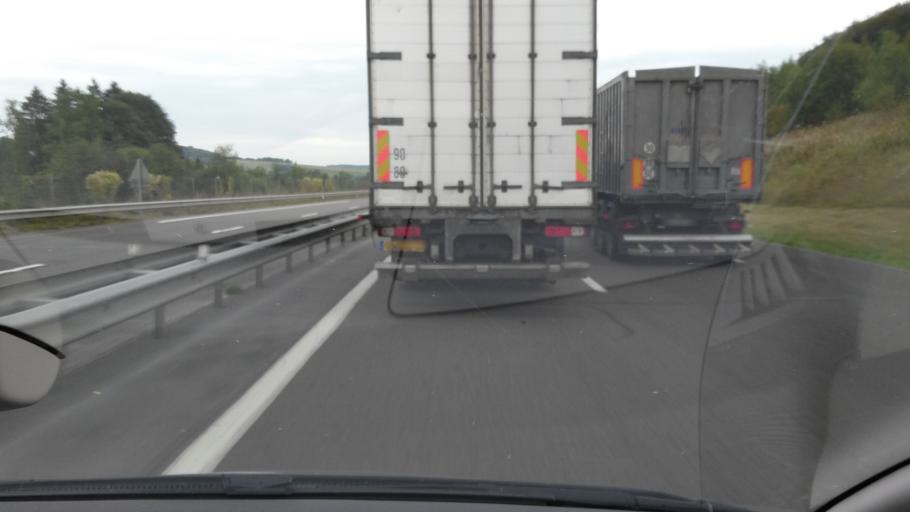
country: FR
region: Champagne-Ardenne
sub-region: Departement des Ardennes
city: La Francheville
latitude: 49.6676
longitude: 4.6436
